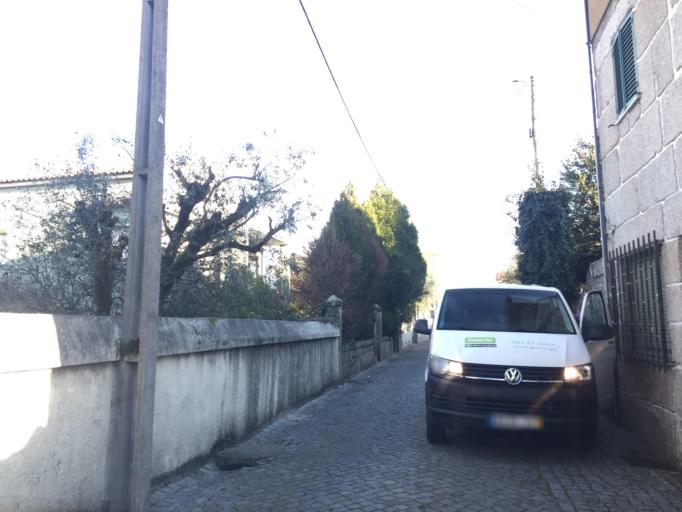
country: PT
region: Viseu
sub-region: Concelho de Carregal do Sal
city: Carregal do Sal
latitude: 40.4733
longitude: -7.9196
